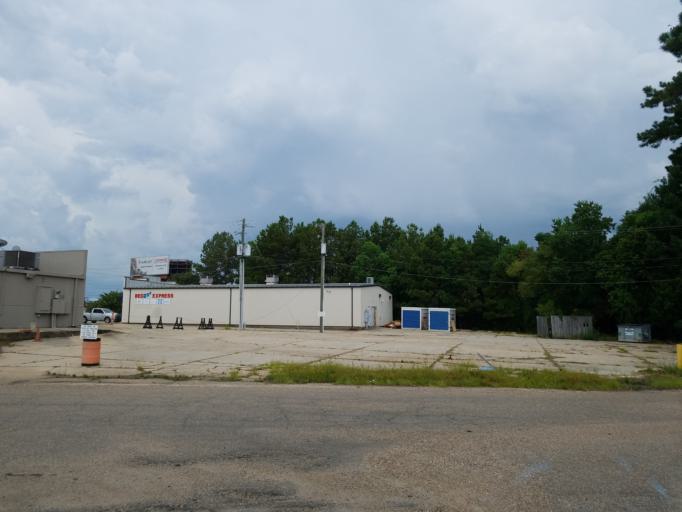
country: US
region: Mississippi
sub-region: Lamar County
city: West Hattiesburg
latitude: 31.3254
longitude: -89.3590
